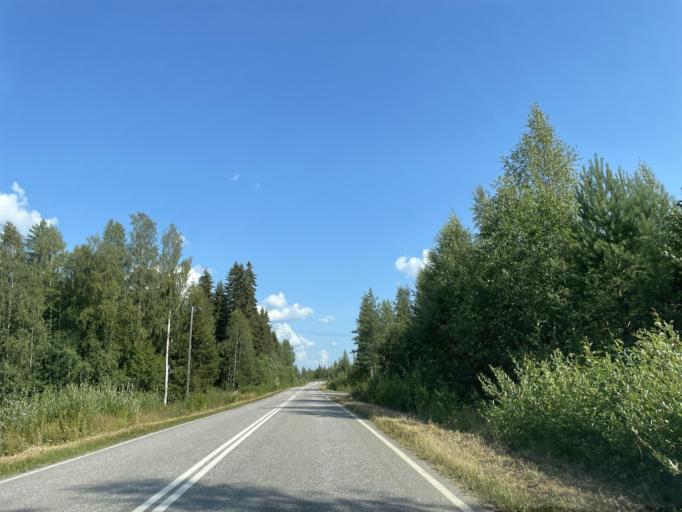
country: FI
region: Central Finland
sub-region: Saarijaervi-Viitasaari
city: Pihtipudas
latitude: 63.3550
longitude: 25.7623
